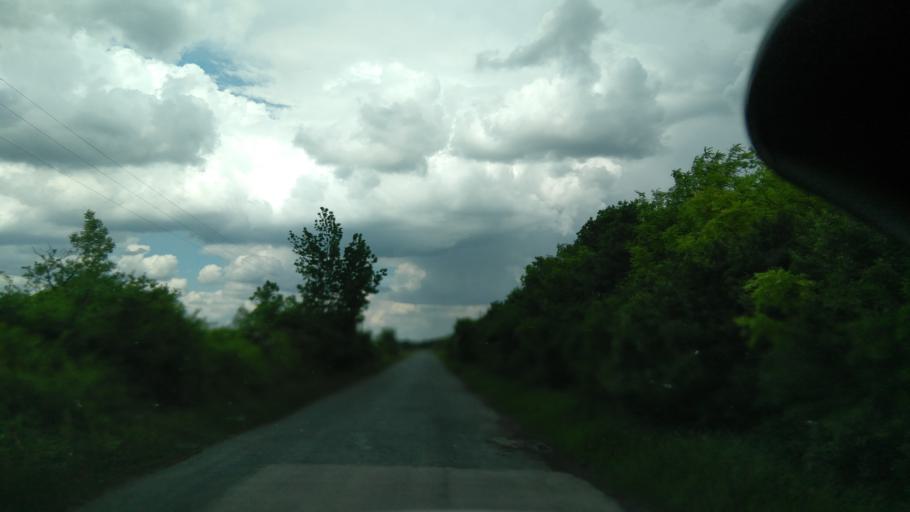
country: HU
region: Bekes
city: Szeghalom
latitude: 47.1022
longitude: 21.0791
